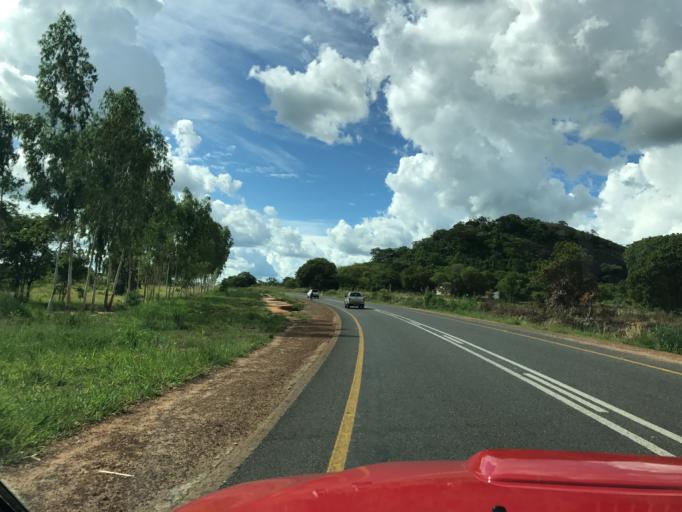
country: MZ
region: Nampula
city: Nampula
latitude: -15.0421
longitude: 39.1374
